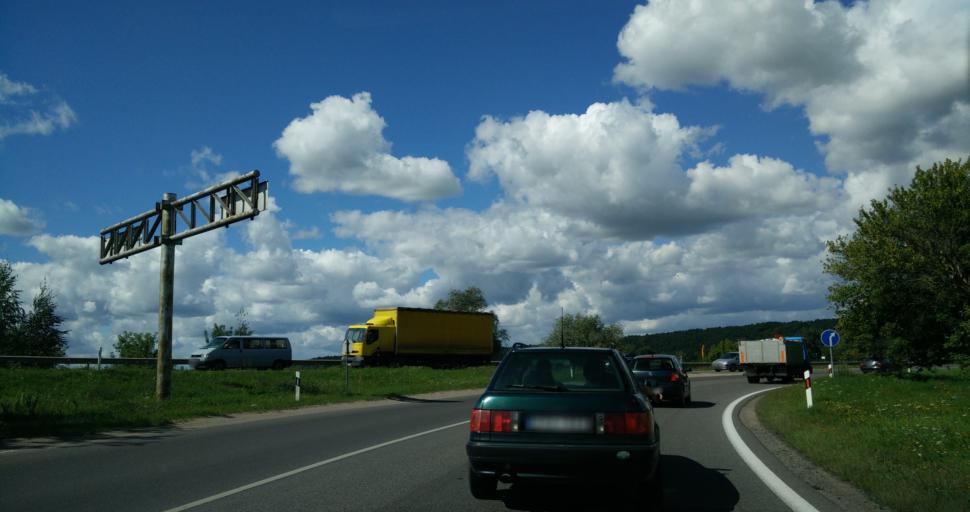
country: LT
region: Kauno apskritis
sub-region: Kauno rajonas
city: Akademija (Kaunas)
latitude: 54.9125
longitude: 23.8339
